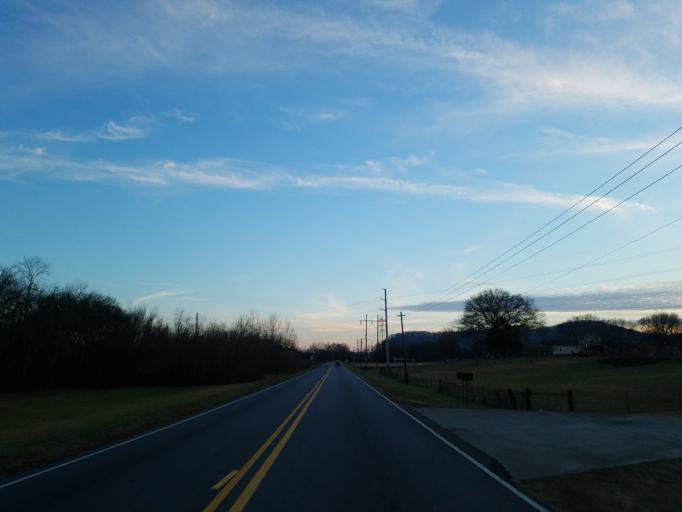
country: US
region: Georgia
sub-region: Bartow County
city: Cartersville
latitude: 34.1752
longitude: -84.8288
